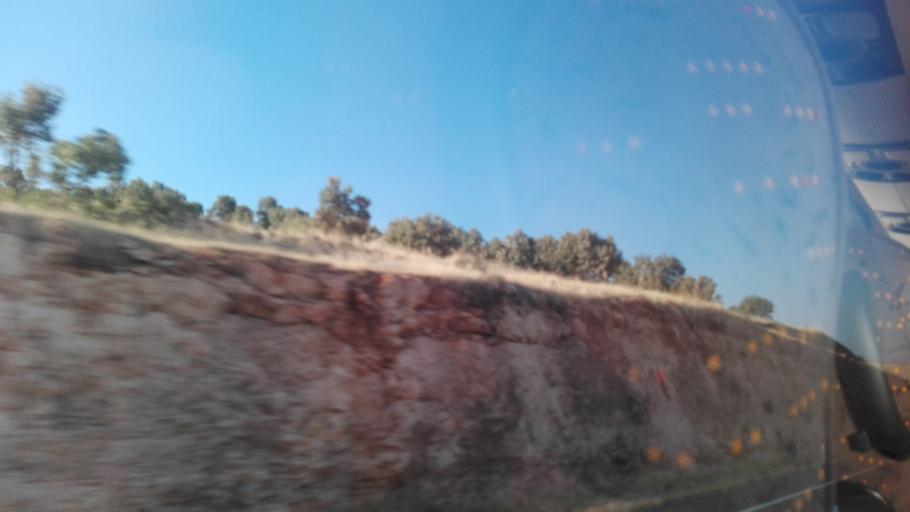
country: TR
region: Mardin
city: Ortaca
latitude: 37.5234
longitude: 41.5912
